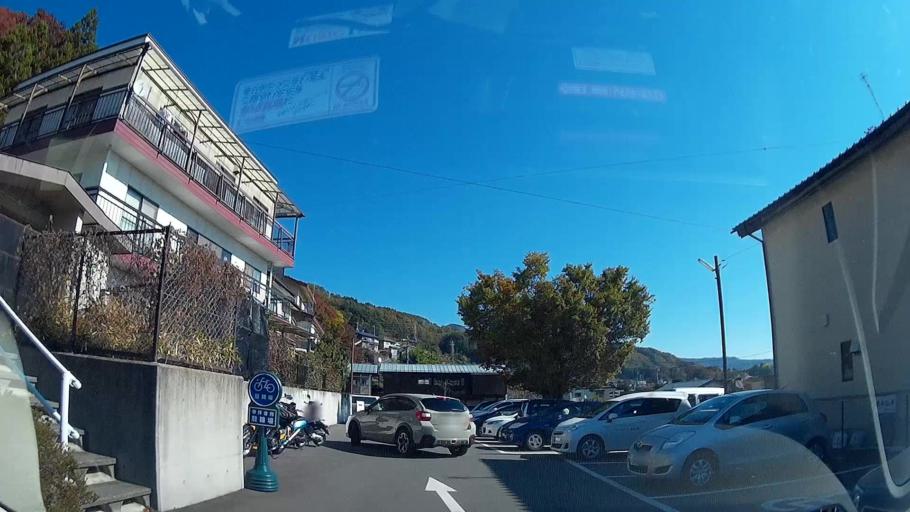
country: JP
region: Nagano
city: Okaya
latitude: 36.0809
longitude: 138.0821
